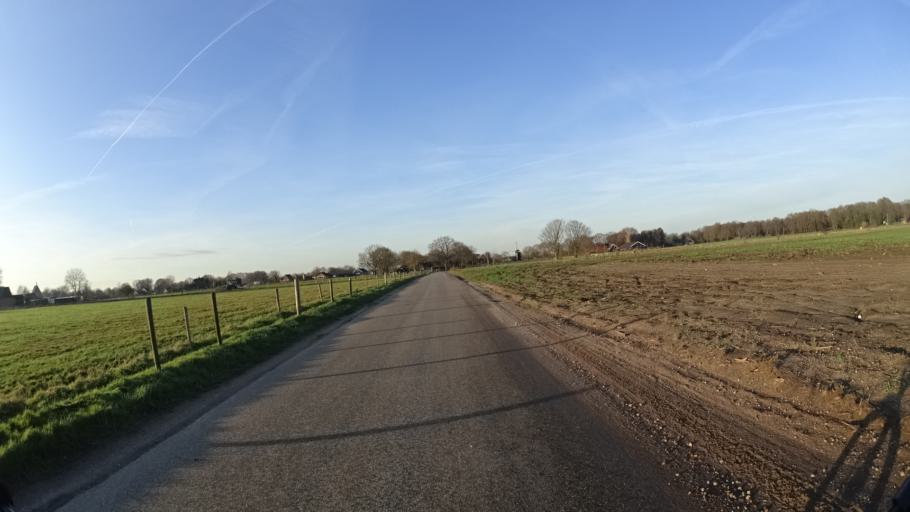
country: NL
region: Gelderland
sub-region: Gemeente Ede
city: Ede
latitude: 52.0581
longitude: 5.6516
